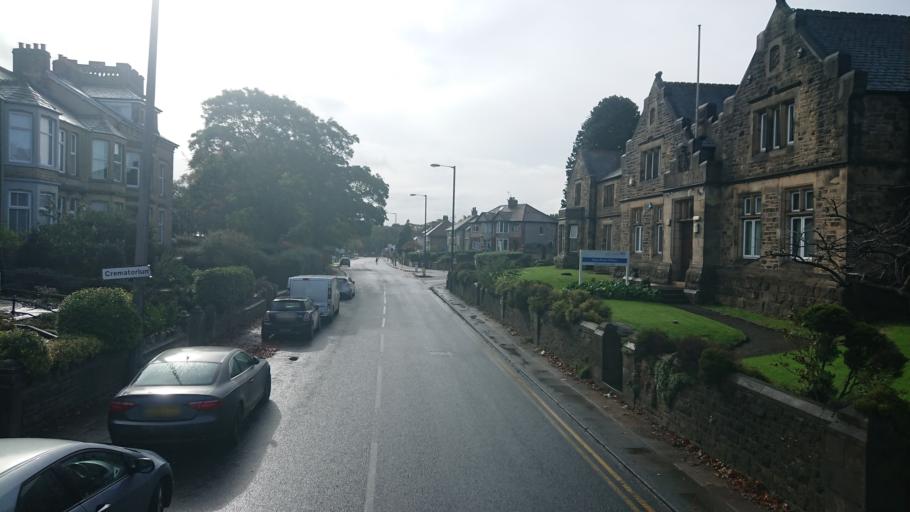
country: GB
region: England
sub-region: Lancashire
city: Lancaster
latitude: 54.0612
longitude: -2.8013
